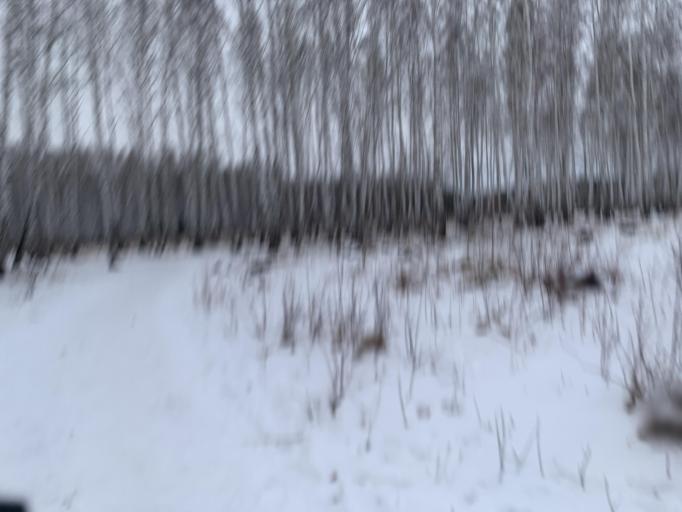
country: RU
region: Chelyabinsk
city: Roshchino
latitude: 55.2035
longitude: 61.2625
